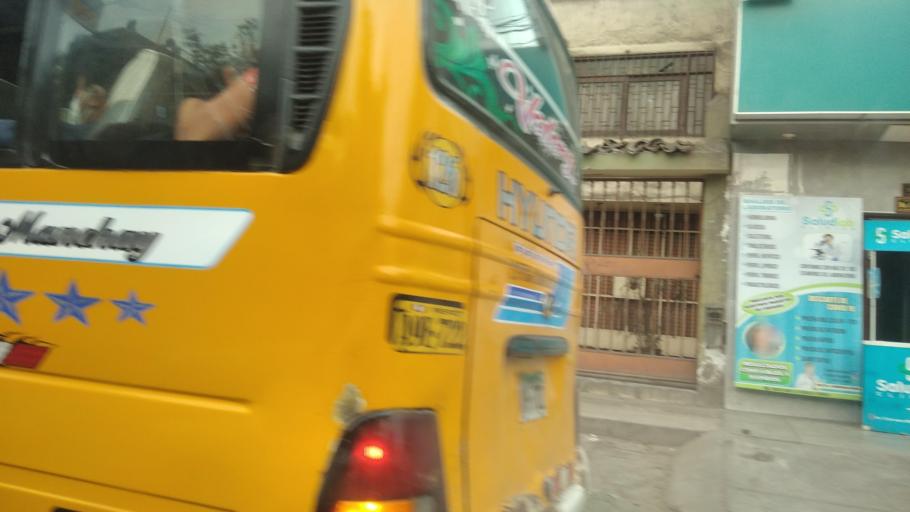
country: PE
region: Lima
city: Lima
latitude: -12.0152
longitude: -76.9970
